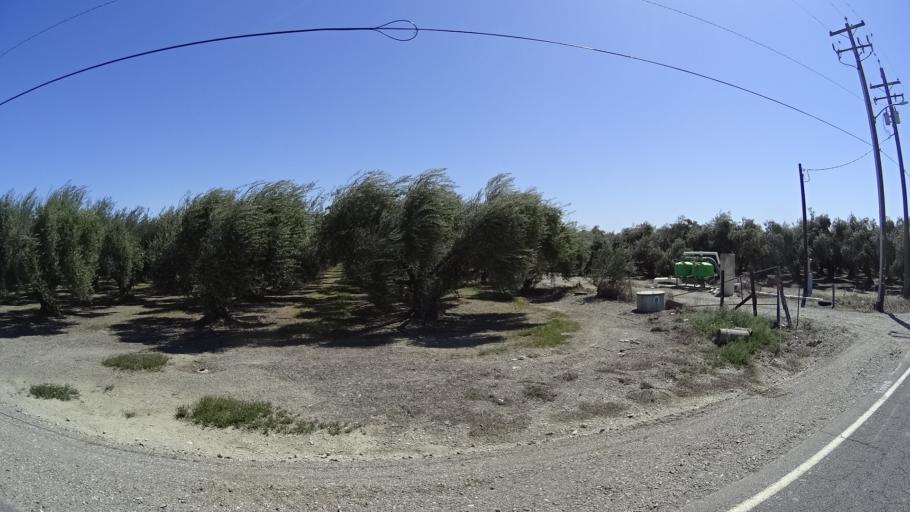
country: US
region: California
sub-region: Glenn County
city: Orland
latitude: 39.7179
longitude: -122.1410
